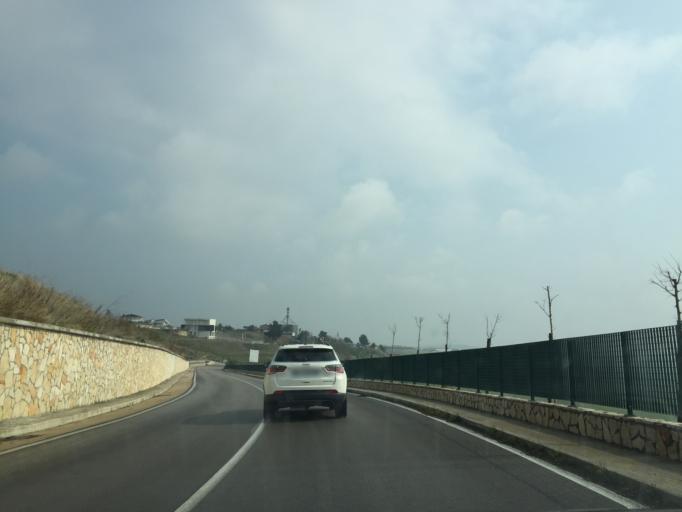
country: IT
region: Apulia
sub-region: Provincia di Foggia
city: Troia
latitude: 41.3657
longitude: 15.3249
